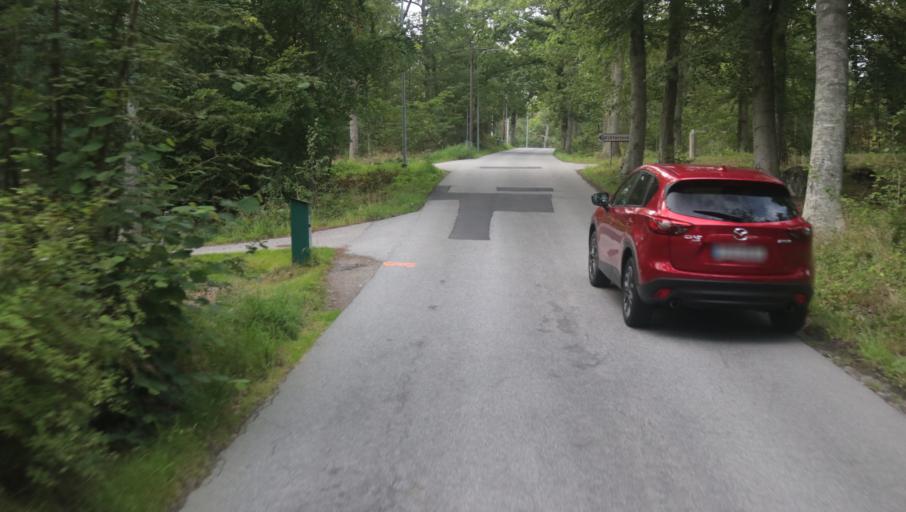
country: SE
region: Blekinge
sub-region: Karlshamns Kommun
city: Karlshamn
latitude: 56.1570
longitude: 14.8808
